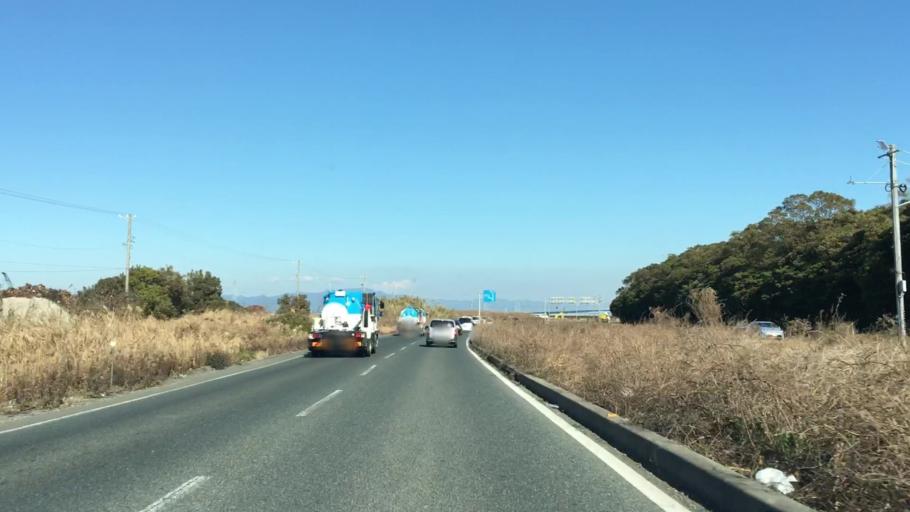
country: JP
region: Aichi
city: Toyohashi
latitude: 34.7219
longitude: 137.3419
